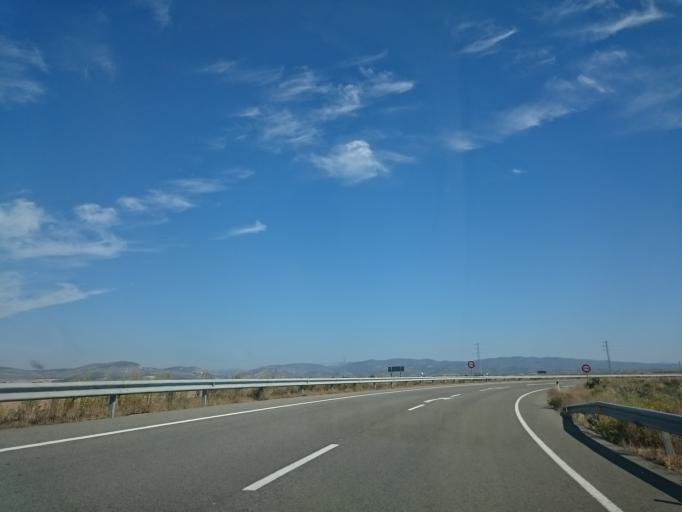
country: ES
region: Catalonia
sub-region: Provincia de Lleida
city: Almenar
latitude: 41.8000
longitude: 0.5548
